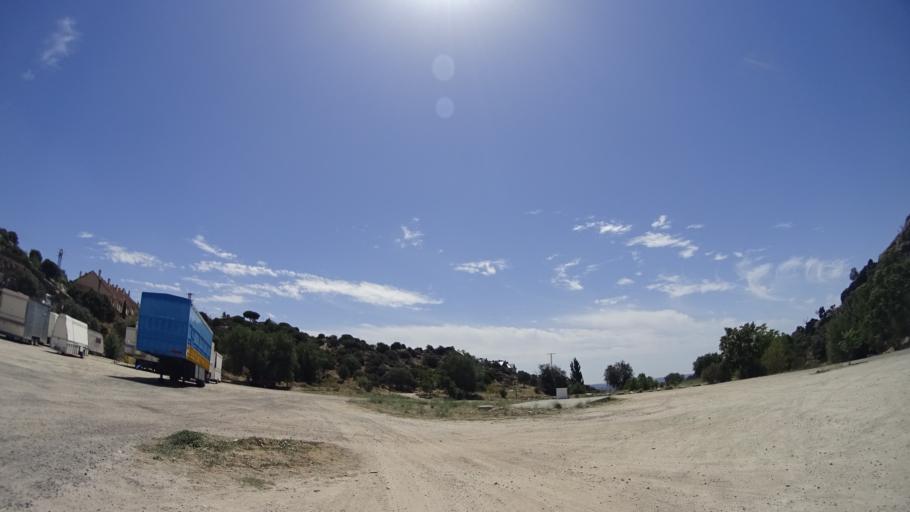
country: ES
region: Madrid
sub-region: Provincia de Madrid
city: Torrelodones
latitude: 40.5724
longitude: -3.9308
